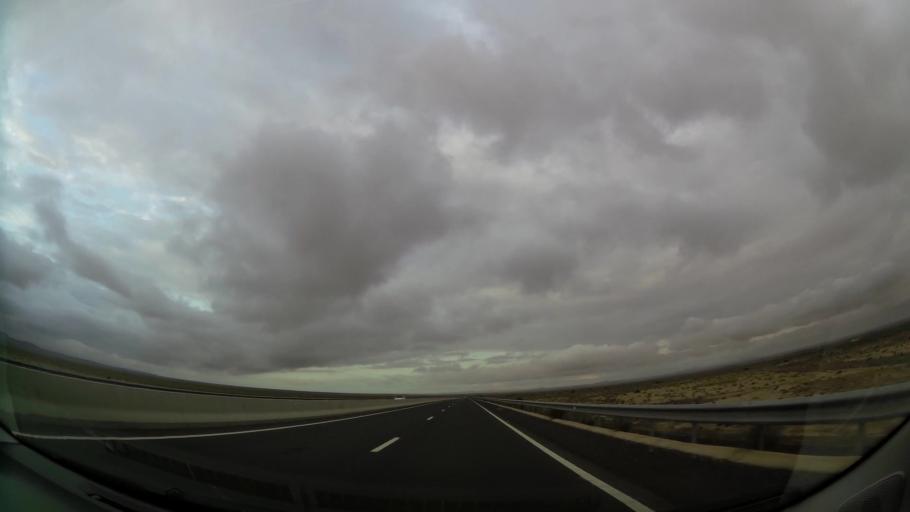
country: MA
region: Taza-Al Hoceima-Taounate
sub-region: Taza
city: Guercif
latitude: 34.3651
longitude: -3.2846
